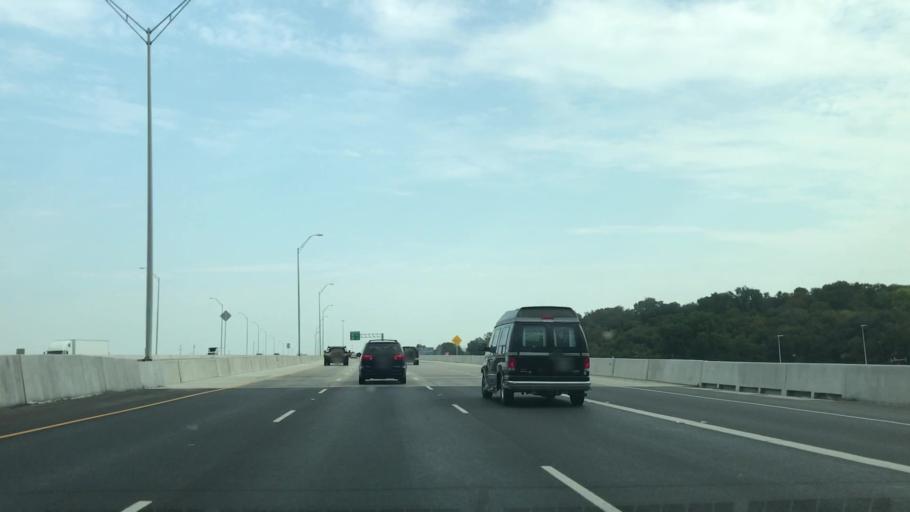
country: US
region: Texas
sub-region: Tarrant County
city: Haltom City
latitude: 32.7844
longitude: -97.3205
